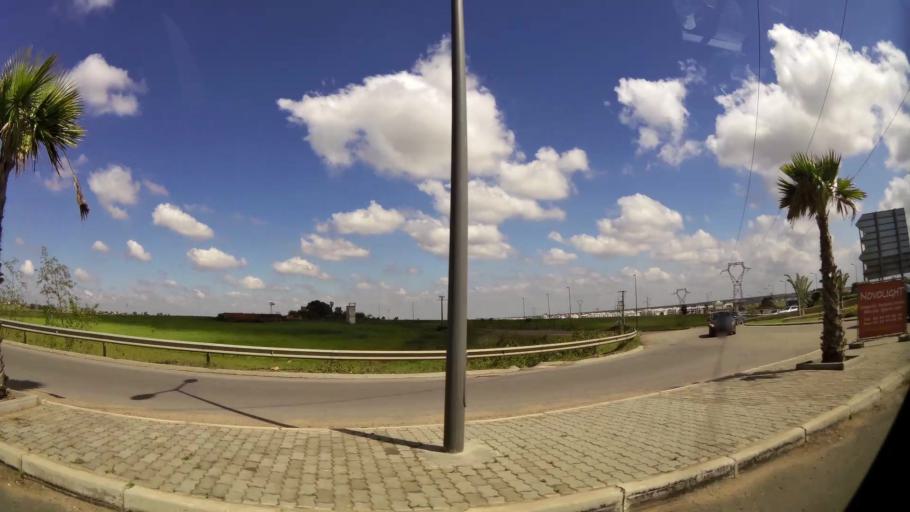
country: MA
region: Grand Casablanca
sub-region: Nouaceur
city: Bouskoura
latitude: 33.5010
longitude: -7.6083
